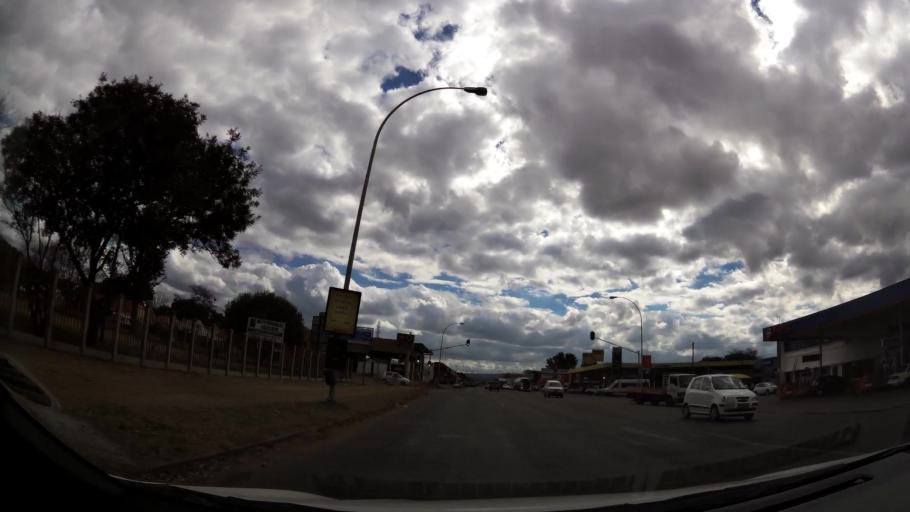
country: ZA
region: Limpopo
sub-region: Waterberg District Municipality
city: Modimolle
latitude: -24.7067
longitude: 28.4119
